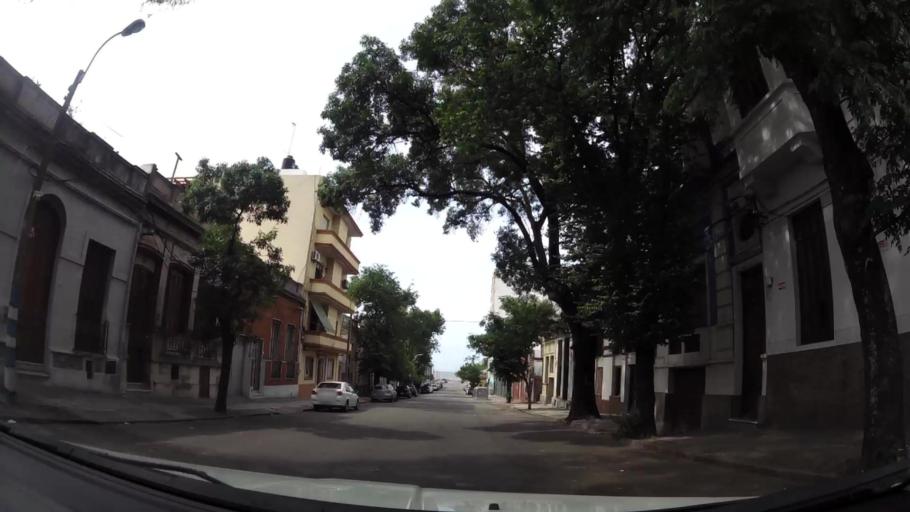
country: UY
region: Montevideo
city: Montevideo
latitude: -34.9126
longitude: -56.1847
